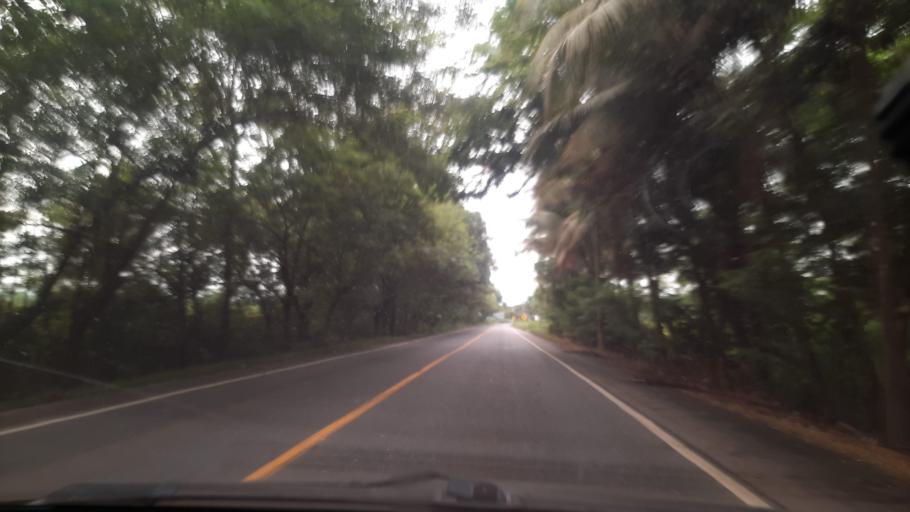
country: GT
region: Izabal
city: Morales
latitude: 15.4530
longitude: -88.9360
